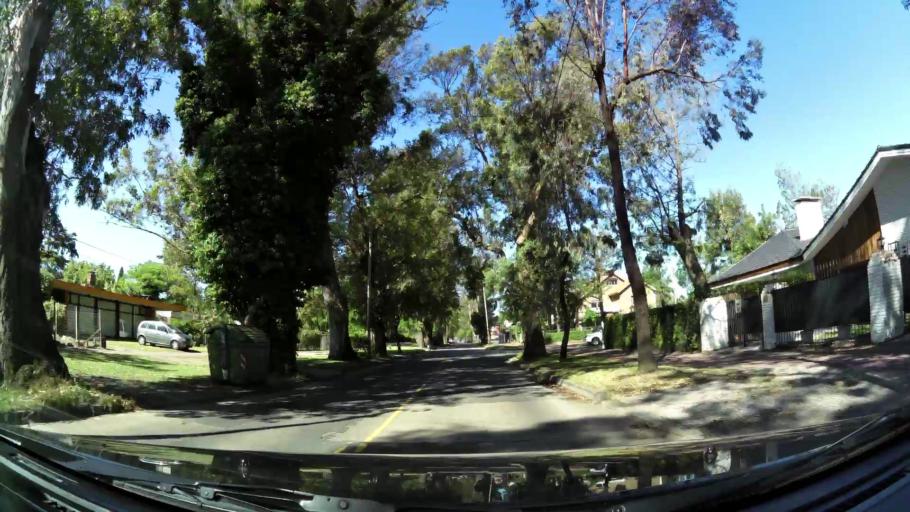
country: UY
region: Canelones
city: Paso de Carrasco
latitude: -34.8880
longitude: -56.0638
